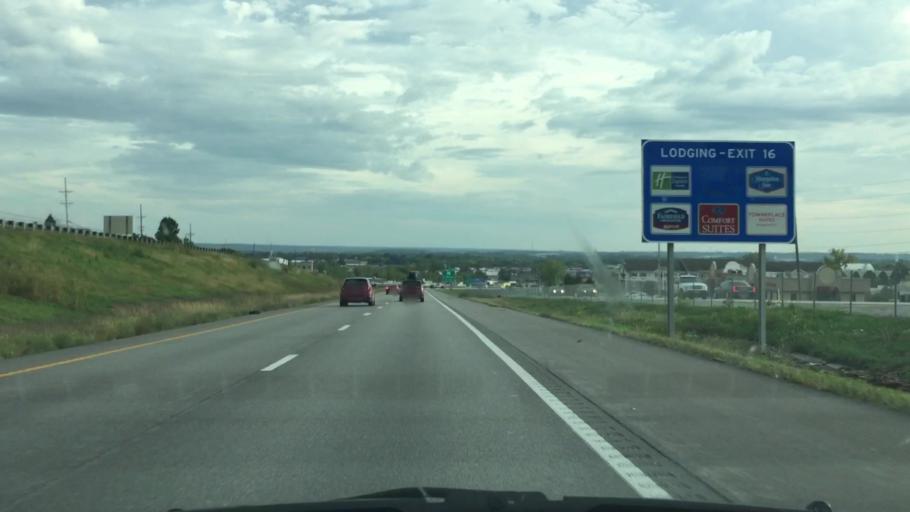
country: US
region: Missouri
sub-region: Clay County
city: Liberty
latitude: 39.2576
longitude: -94.4500
